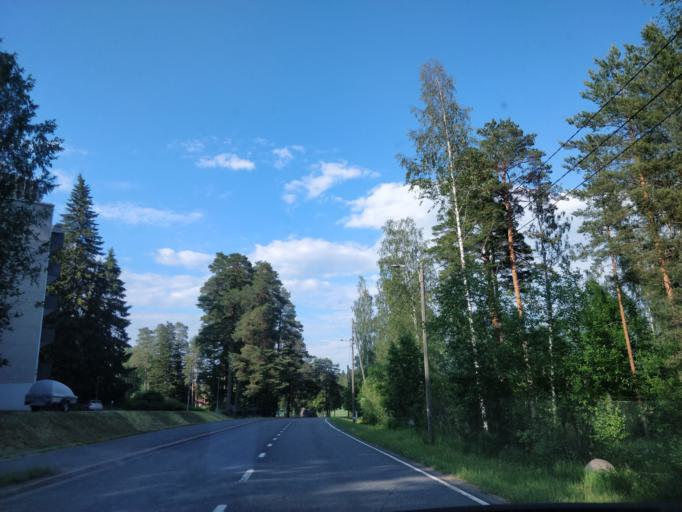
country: FI
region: Haeme
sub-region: Haemeenlinna
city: Tervakoski
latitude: 60.8092
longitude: 24.6122
